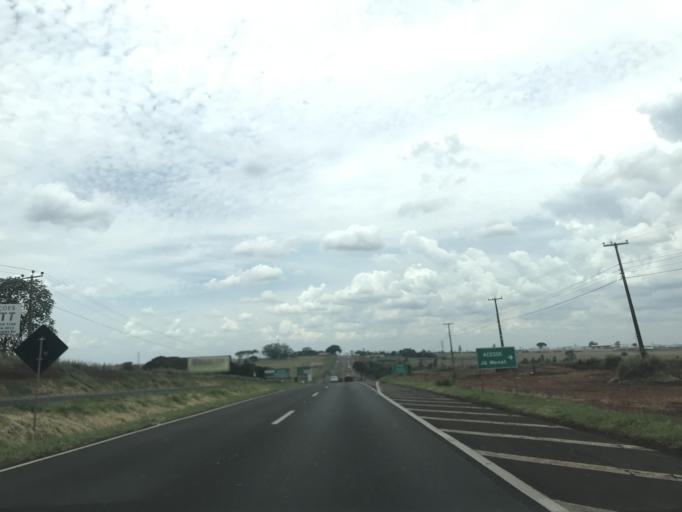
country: BR
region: Parana
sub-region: Paicandu
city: Paicandu
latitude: -23.3919
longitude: -52.0117
